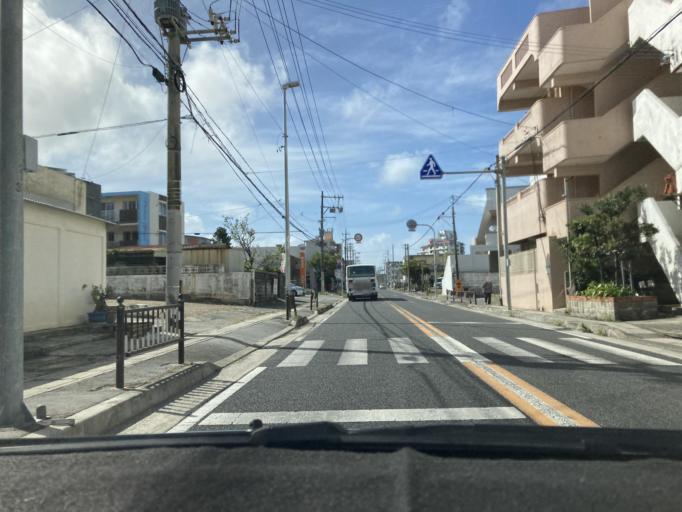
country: JP
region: Okinawa
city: Itoman
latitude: 26.1232
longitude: 127.6700
